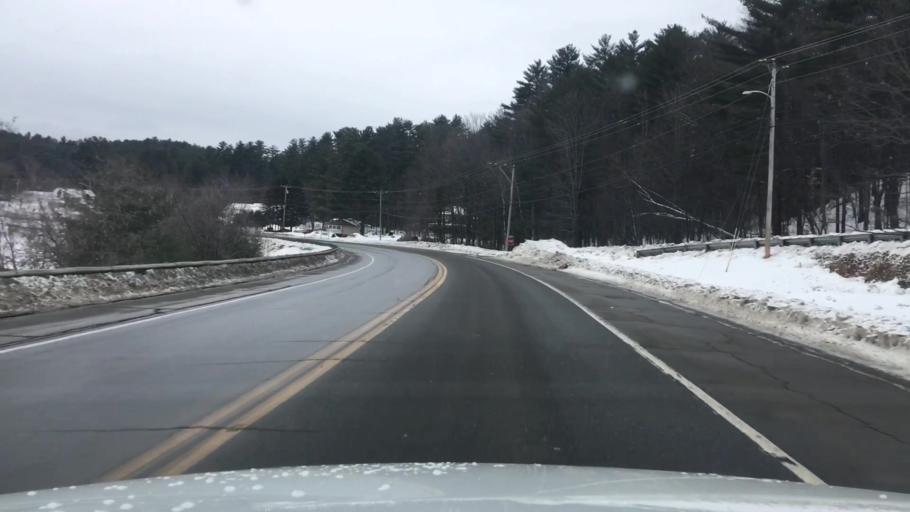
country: US
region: Maine
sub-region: Somerset County
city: Skowhegan
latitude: 44.7724
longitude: -69.7039
